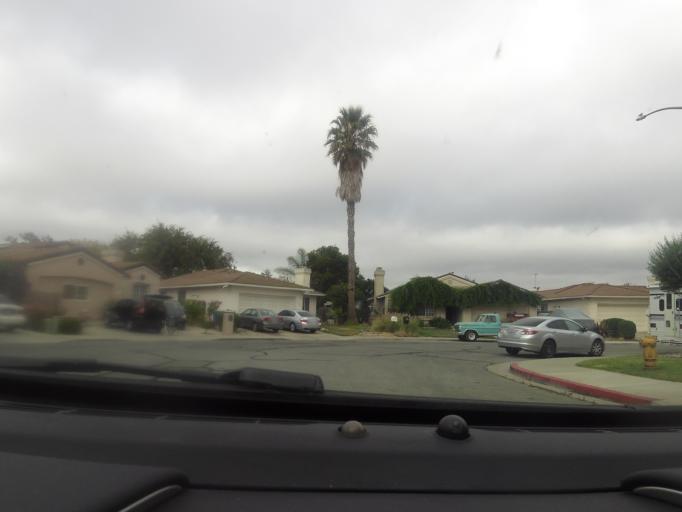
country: US
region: California
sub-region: San Benito County
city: Hollister
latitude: 36.8437
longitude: -121.4156
